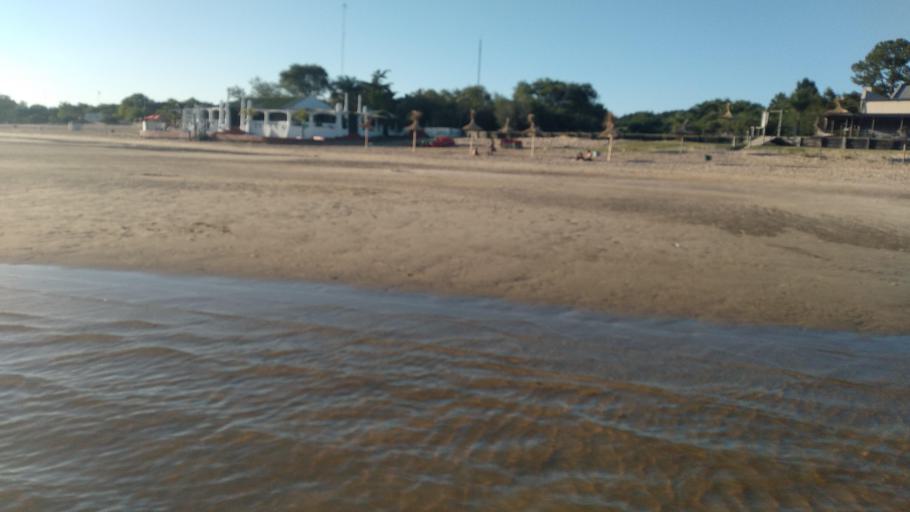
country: UY
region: Rio Negro
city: Fray Bentos
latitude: -33.0678
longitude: -58.3876
